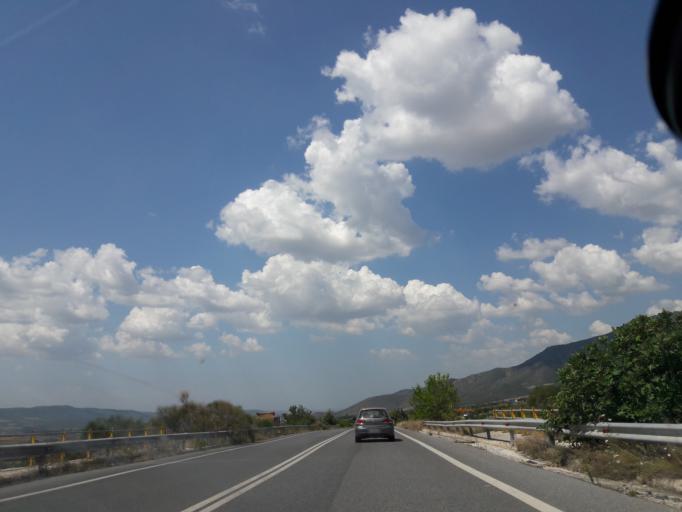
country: GR
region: Central Macedonia
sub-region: Nomos Chalkidikis
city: Galatista
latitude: 40.4637
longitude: 23.2678
